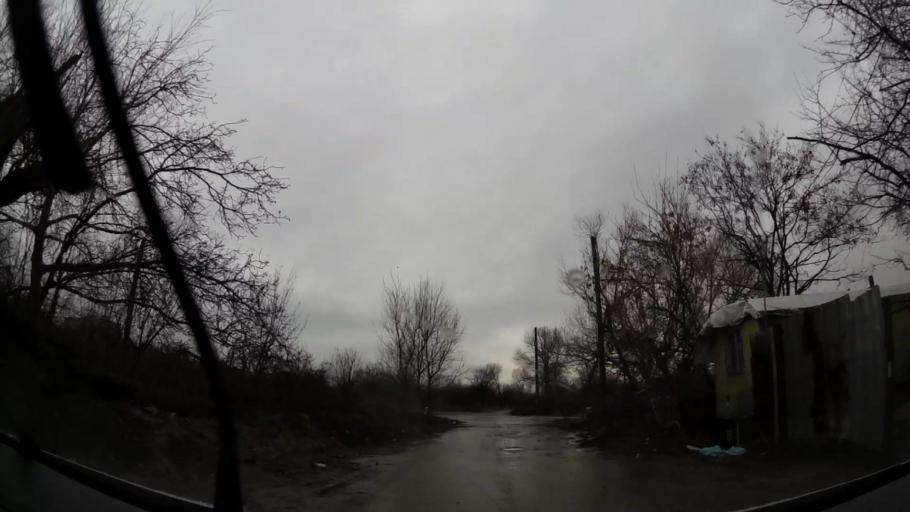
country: BG
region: Sofia-Capital
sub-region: Stolichna Obshtina
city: Sofia
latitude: 42.6500
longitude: 23.3287
